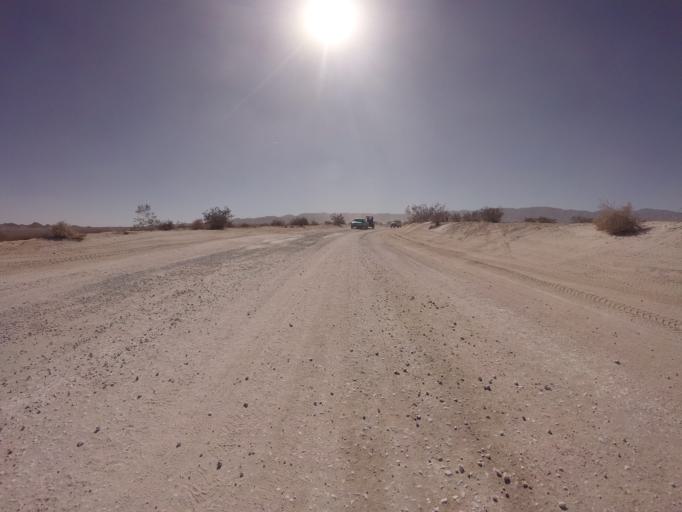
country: US
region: California
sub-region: San Bernardino County
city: Yucca Valley
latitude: 34.3837
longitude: -116.5427
